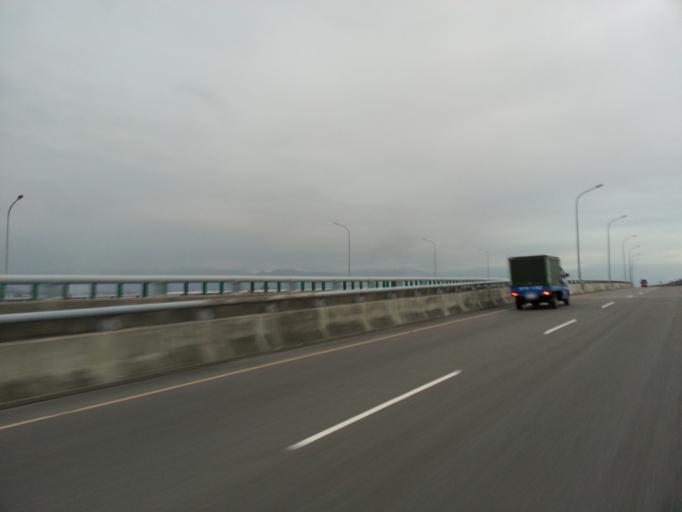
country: TW
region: Taiwan
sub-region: Yilan
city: Yilan
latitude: 24.6576
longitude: 121.8034
